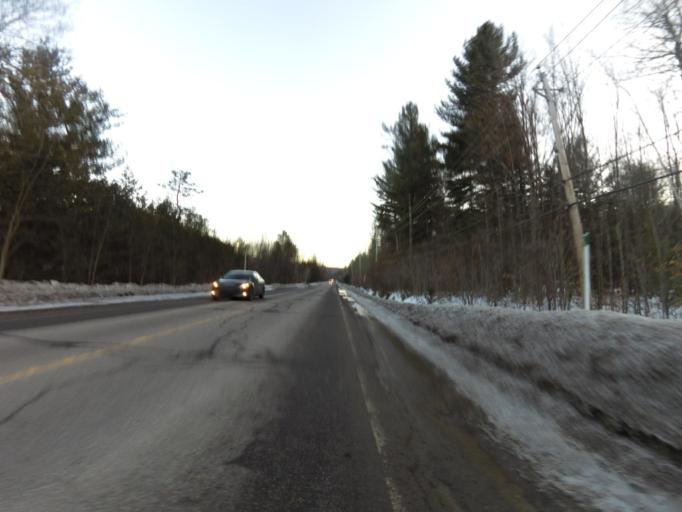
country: CA
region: Quebec
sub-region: Outaouais
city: Gatineau
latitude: 45.4960
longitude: -75.8141
